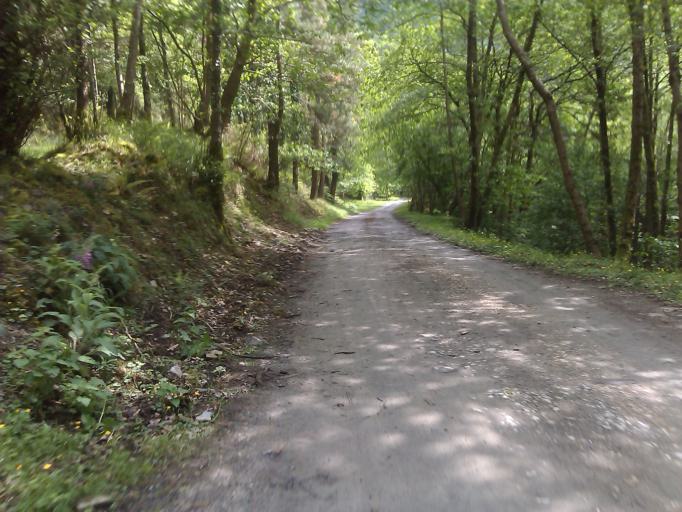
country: ES
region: Basque Country
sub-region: Provincia de Guipuzcoa
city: Berastegui
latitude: 43.1379
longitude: -1.9493
